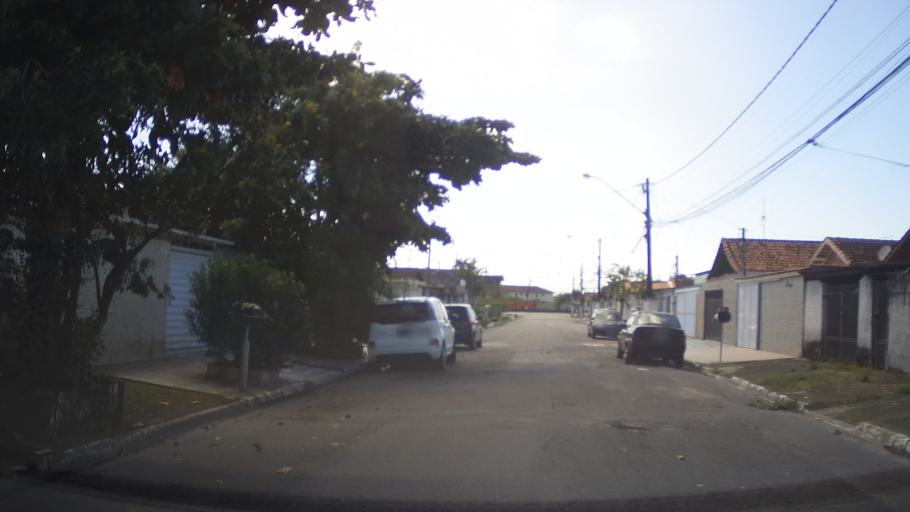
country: BR
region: Sao Paulo
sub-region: Mongagua
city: Mongagua
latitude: -24.0339
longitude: -46.5261
